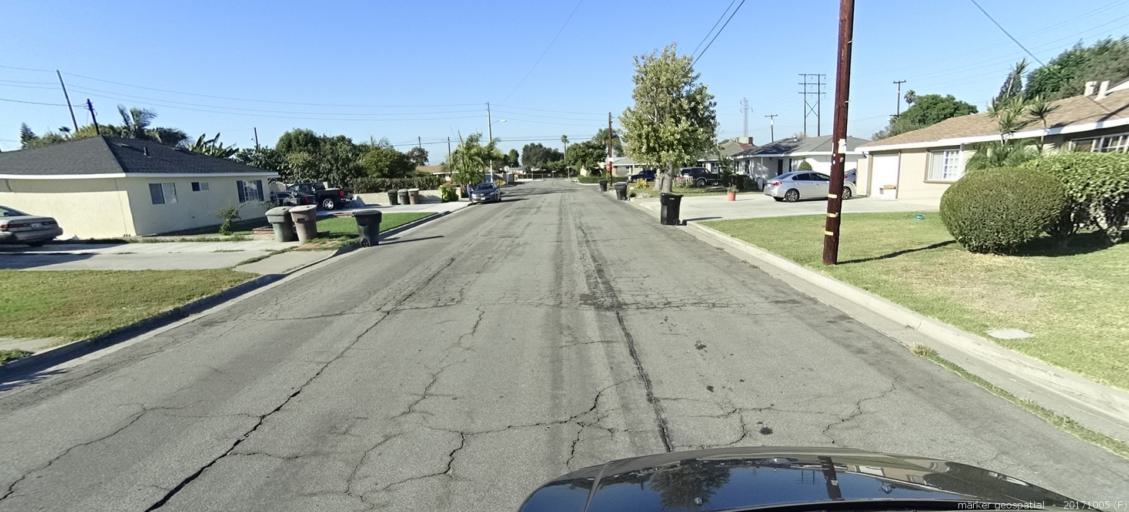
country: US
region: California
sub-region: Orange County
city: Stanton
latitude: 33.7910
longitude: -117.9803
